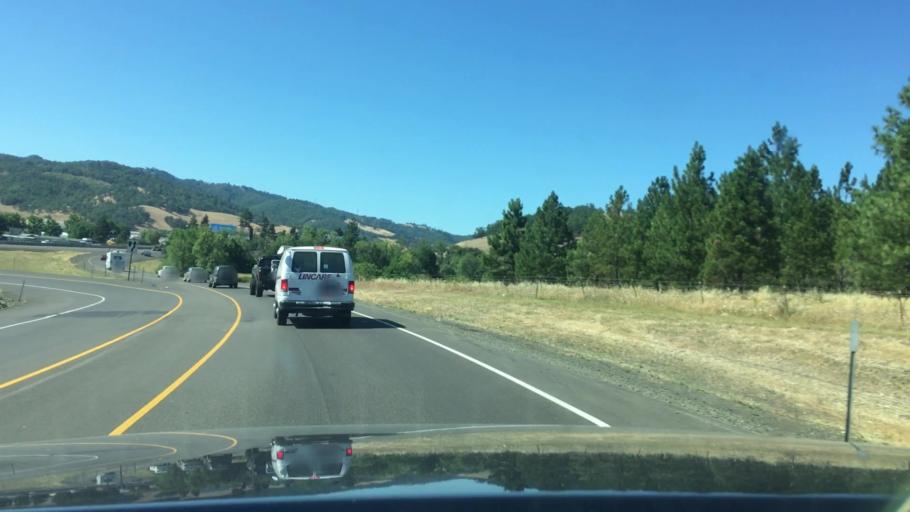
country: US
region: Oregon
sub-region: Douglas County
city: Green
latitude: 43.1561
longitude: -123.3631
